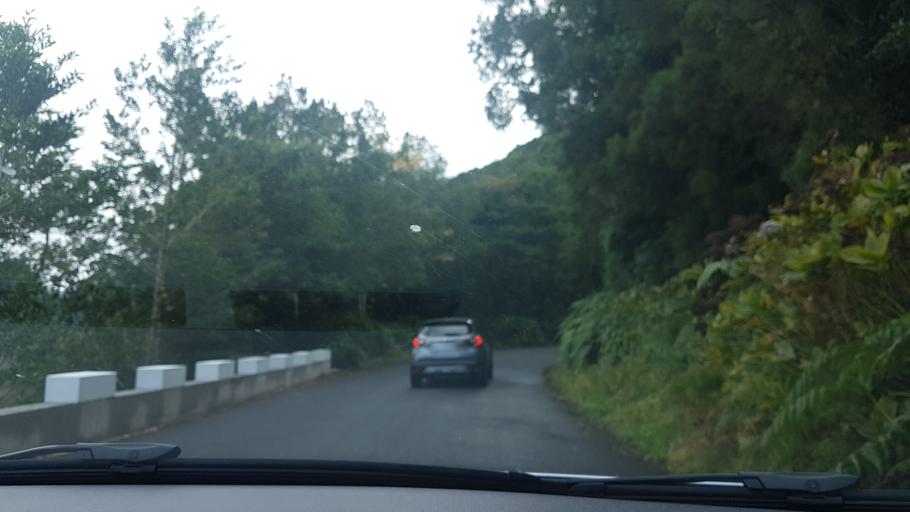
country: PT
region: Madeira
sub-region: Sao Vicente
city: Sao Vicente
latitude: 32.7625
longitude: -17.0211
